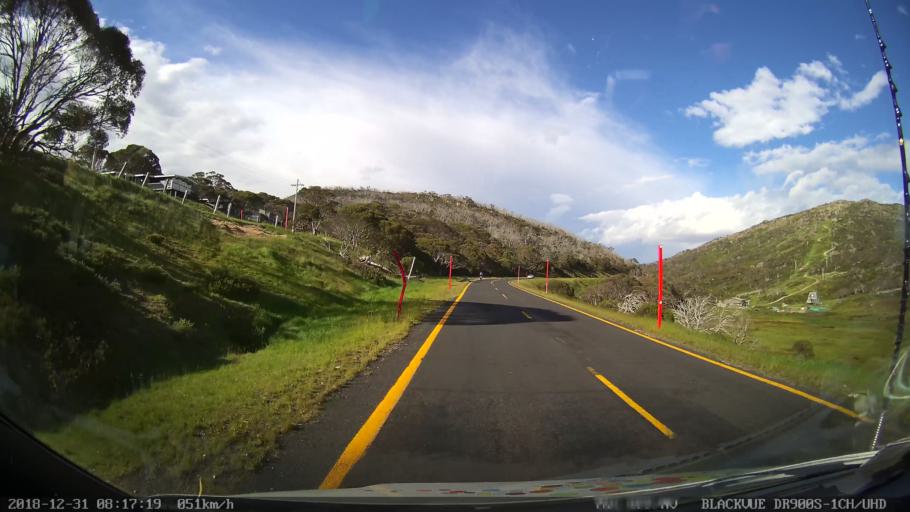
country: AU
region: New South Wales
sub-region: Snowy River
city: Jindabyne
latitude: -36.4100
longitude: 148.4054
